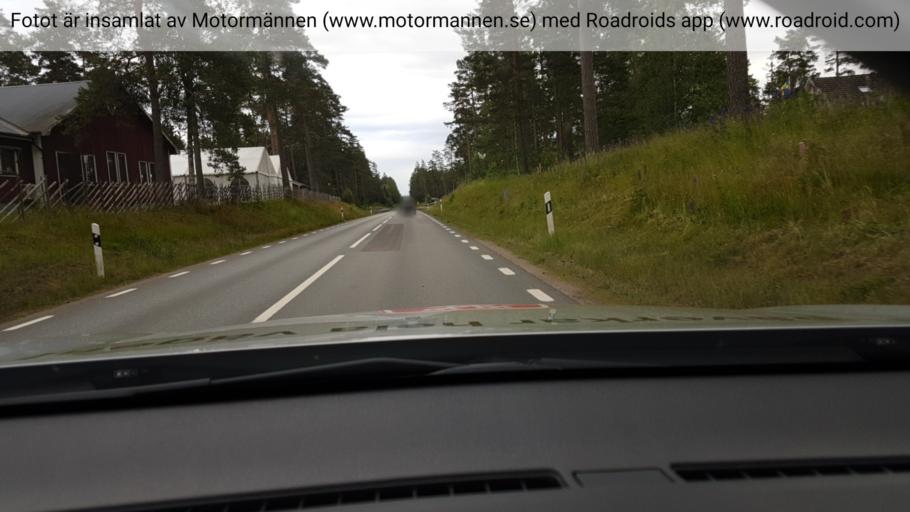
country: SE
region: Joenkoeping
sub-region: Mullsjo Kommun
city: Mullsjoe
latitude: 57.8915
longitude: 13.8439
